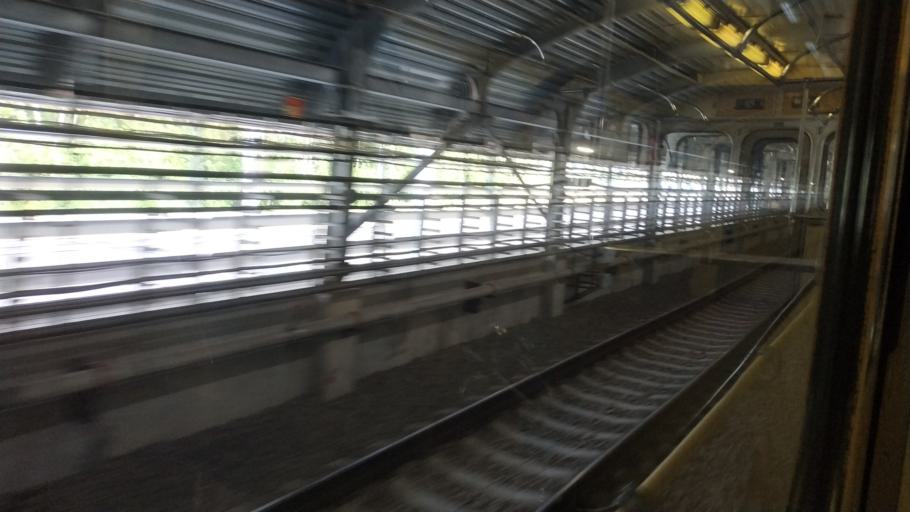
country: RU
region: Moskovskaya
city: Mosrentgen
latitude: 55.5890
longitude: 37.4231
